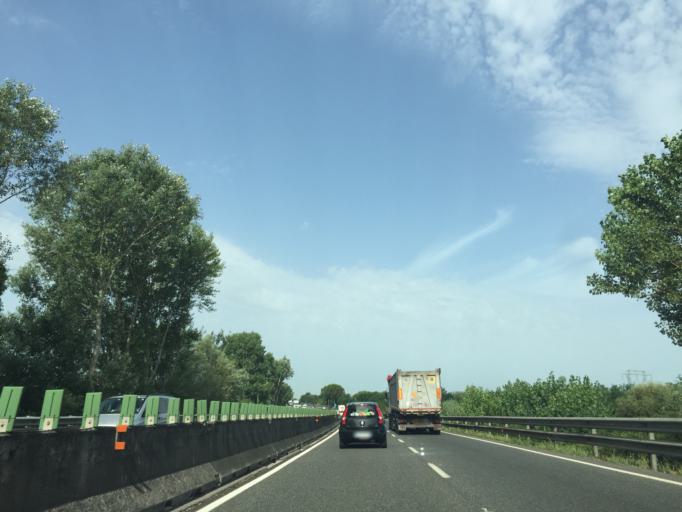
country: IT
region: Tuscany
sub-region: Province of Florence
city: San Pierino
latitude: 43.6987
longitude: 10.8169
